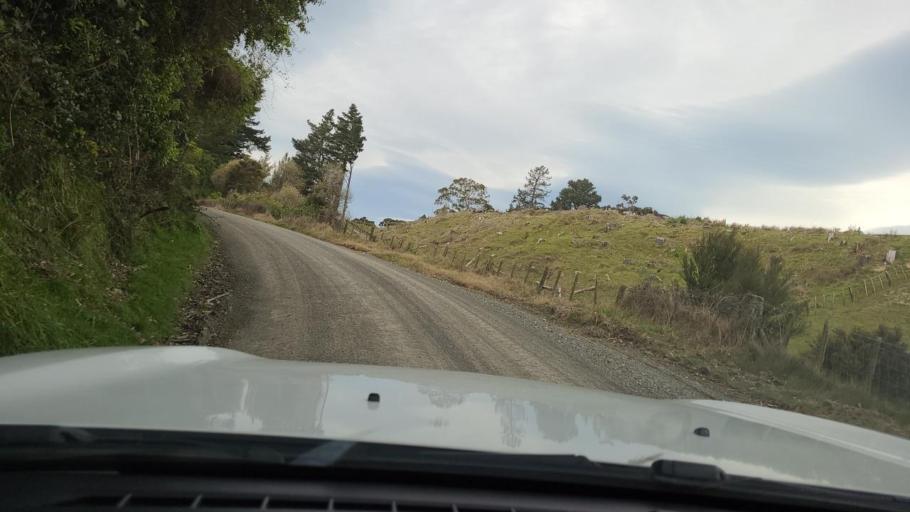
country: NZ
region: Hawke's Bay
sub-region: Napier City
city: Napier
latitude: -39.3010
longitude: 176.8305
